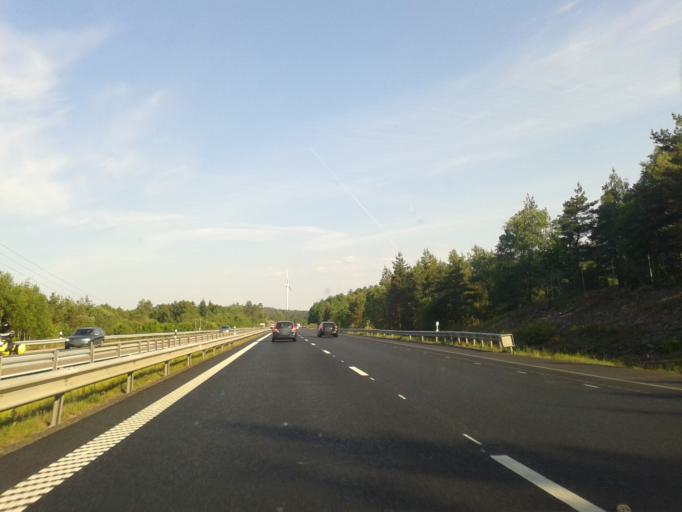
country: SE
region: Vaestra Goetaland
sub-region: Kungalvs Kommun
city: Kode
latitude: 57.9116
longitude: 11.8938
